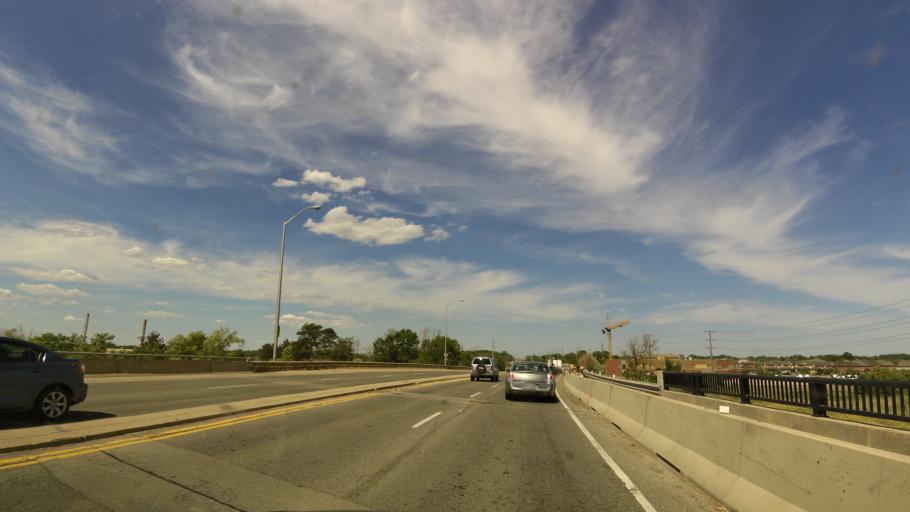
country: CA
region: Ontario
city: Burlington
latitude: 43.4098
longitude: -79.8049
